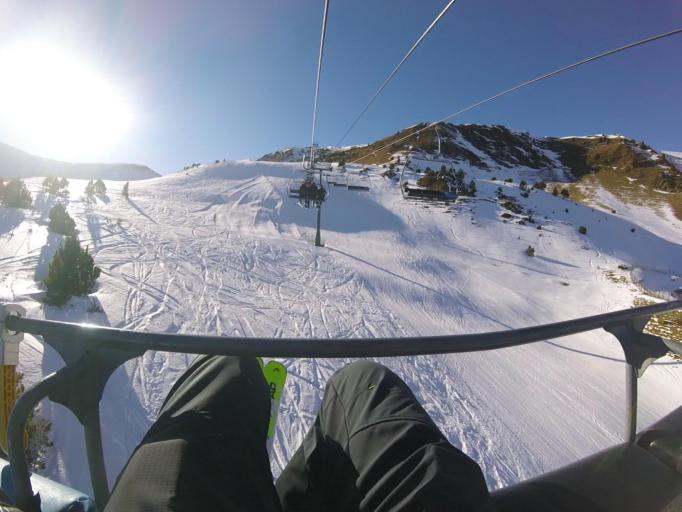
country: AD
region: Canillo
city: El Tarter
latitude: 42.5519
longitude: 1.6570
